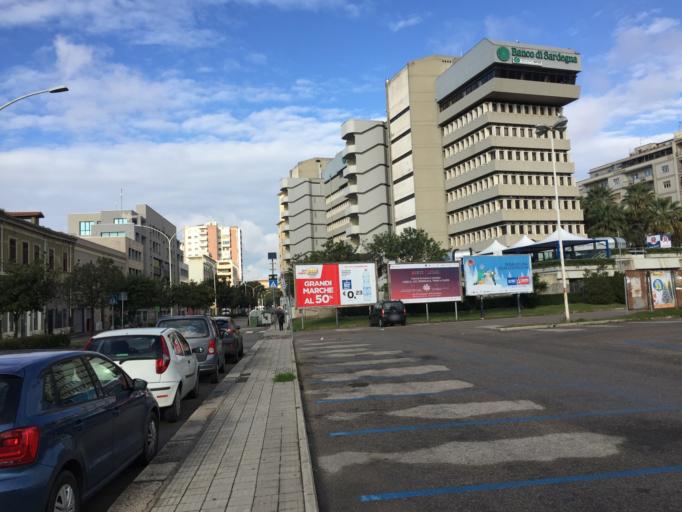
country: IT
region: Sardinia
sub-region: Provincia di Cagliari
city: Cagliari
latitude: 39.2097
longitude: 9.1208
